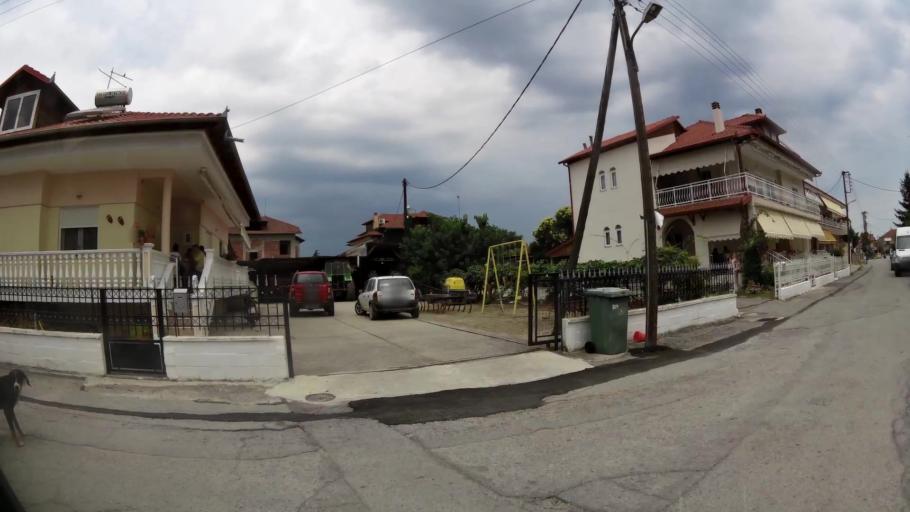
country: GR
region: Central Macedonia
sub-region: Nomos Pierias
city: Kallithea
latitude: 40.2729
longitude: 22.5799
